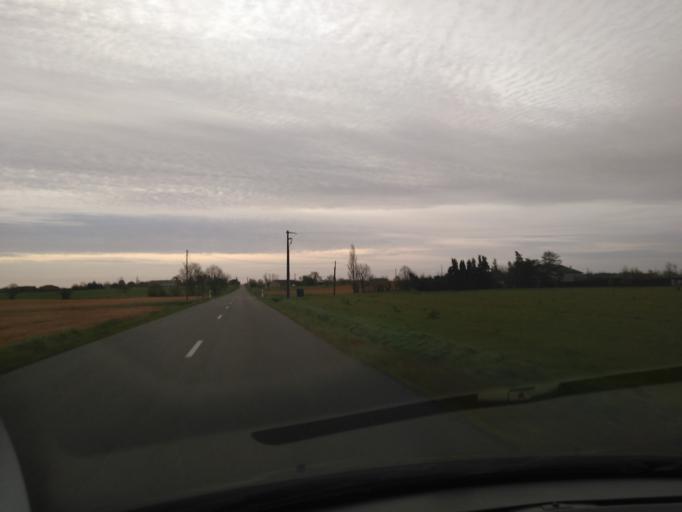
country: FR
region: Midi-Pyrenees
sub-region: Departement du Tarn-et-Garonne
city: Verdun-sur-Garonne
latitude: 43.8285
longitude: 1.1697
